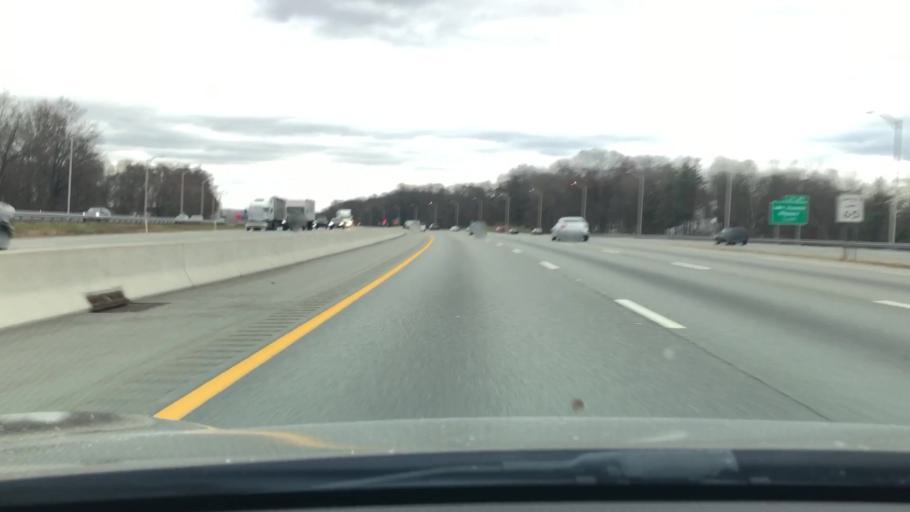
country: US
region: New Jersey
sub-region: Morris County
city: Parsippany
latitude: 40.8607
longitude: -74.3987
